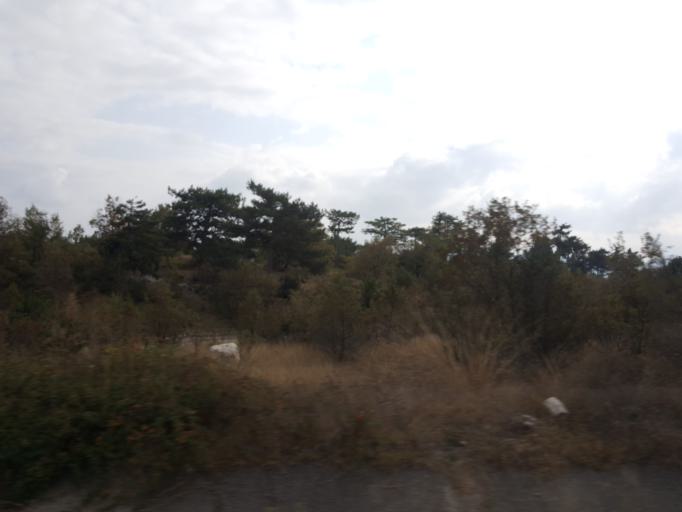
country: TR
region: Sinop
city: Sarayduzu
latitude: 41.3404
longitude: 34.7951
